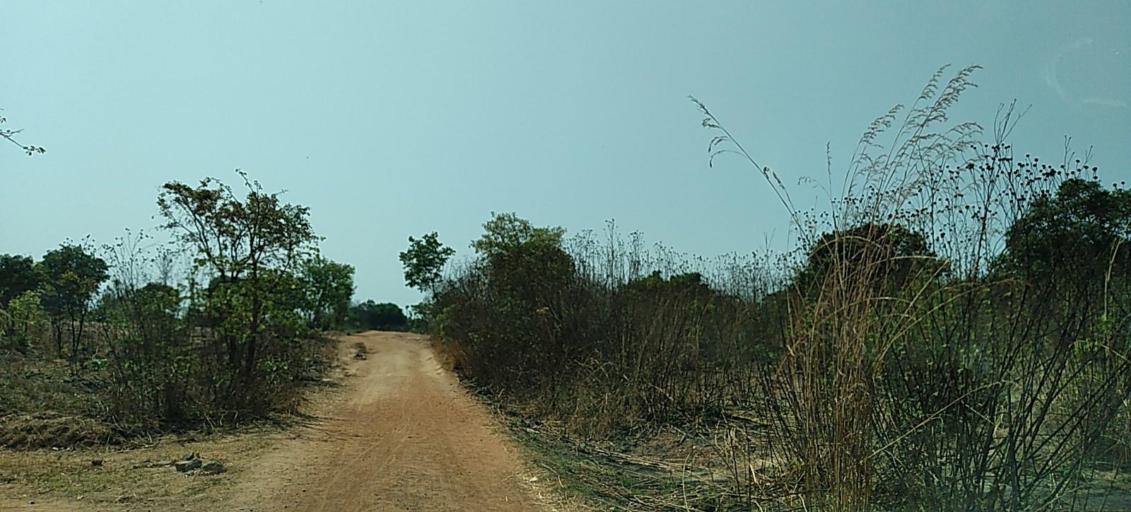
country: ZM
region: Copperbelt
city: Luanshya
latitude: -13.3413
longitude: 28.3906
